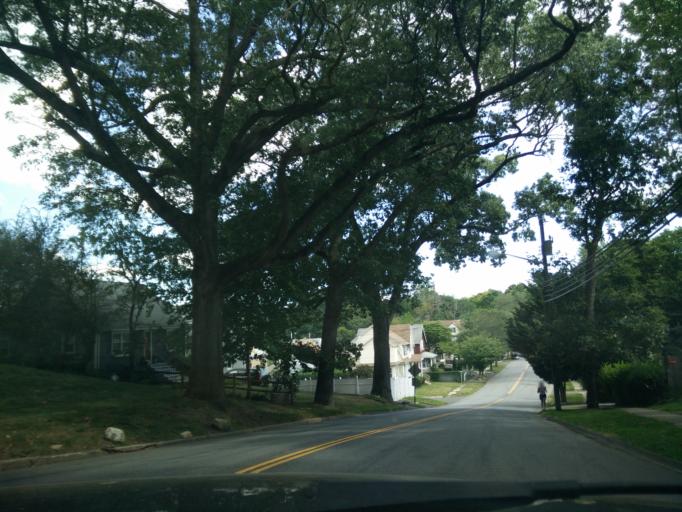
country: US
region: Connecticut
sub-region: Fairfield County
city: Bridgeport
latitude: 41.1810
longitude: -73.2252
